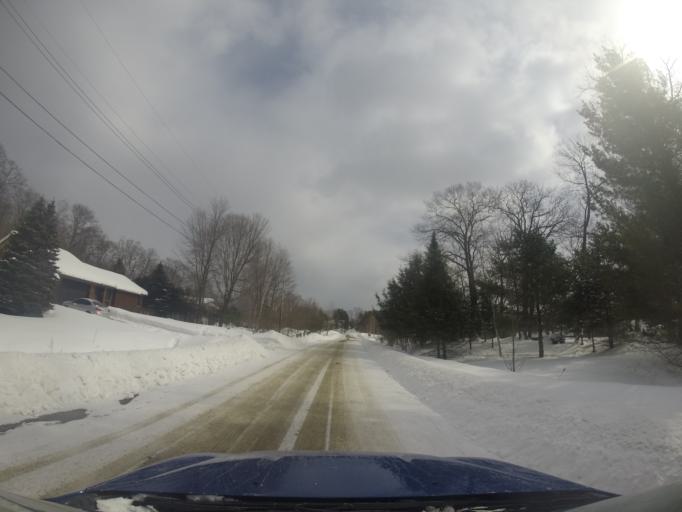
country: CA
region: Ontario
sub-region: Parry Sound District
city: Parry Sound
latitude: 45.3904
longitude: -80.0305
